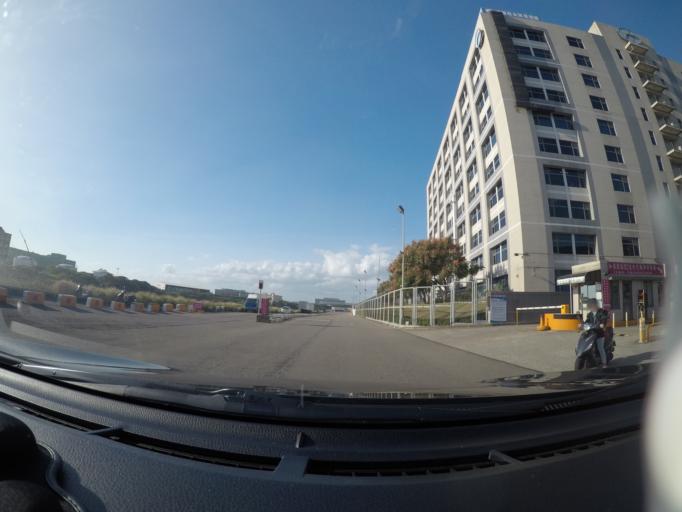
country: TW
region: Taiwan
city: Taoyuan City
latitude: 25.0927
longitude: 121.2533
